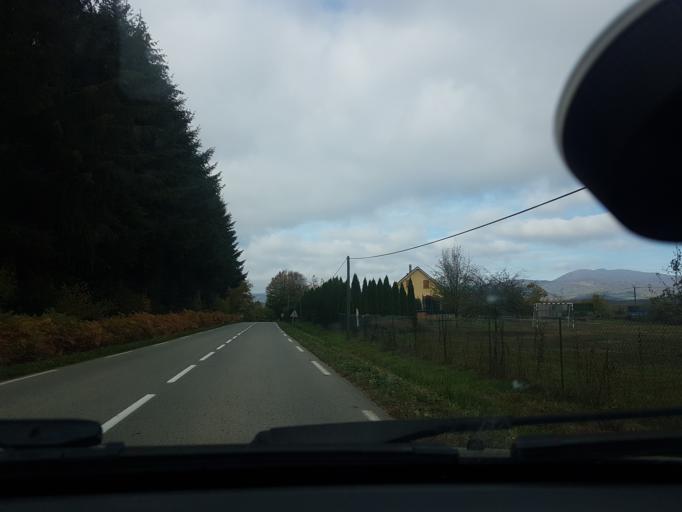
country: FR
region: Franche-Comte
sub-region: Departement de la Haute-Saone
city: Plancher-Bas
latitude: 47.6961
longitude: 6.7359
